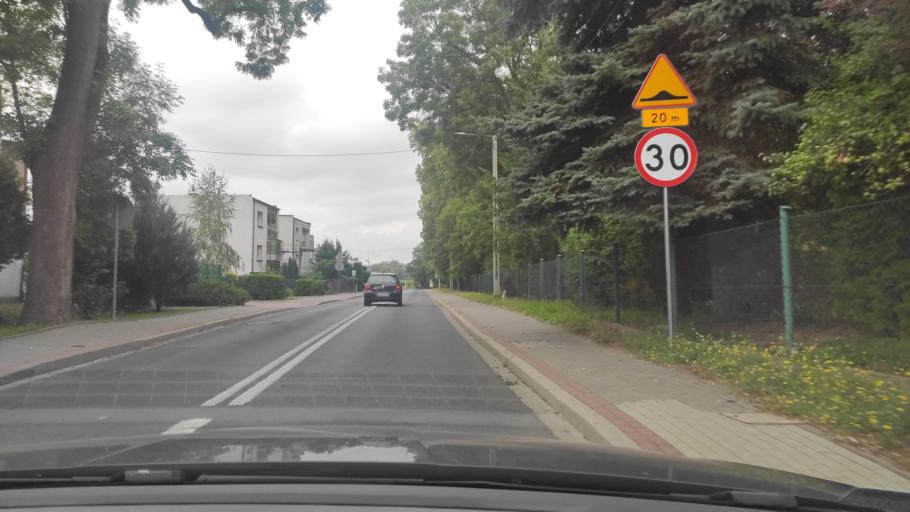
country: PL
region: Greater Poland Voivodeship
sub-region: Powiat poznanski
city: Swarzedz
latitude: 52.4094
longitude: 17.0631
